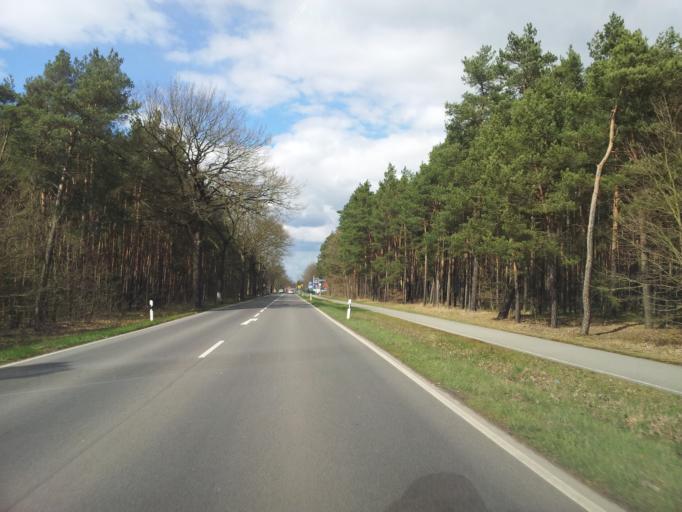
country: DE
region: Saxony
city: Wittichenau
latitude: 51.4171
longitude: 14.2832
